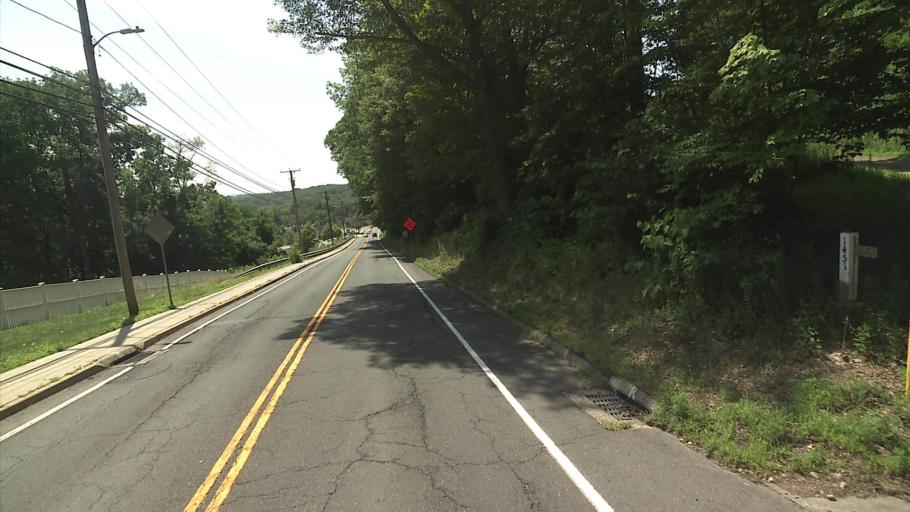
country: US
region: Connecticut
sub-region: Tolland County
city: South Coventry
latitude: 41.7730
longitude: -72.3066
